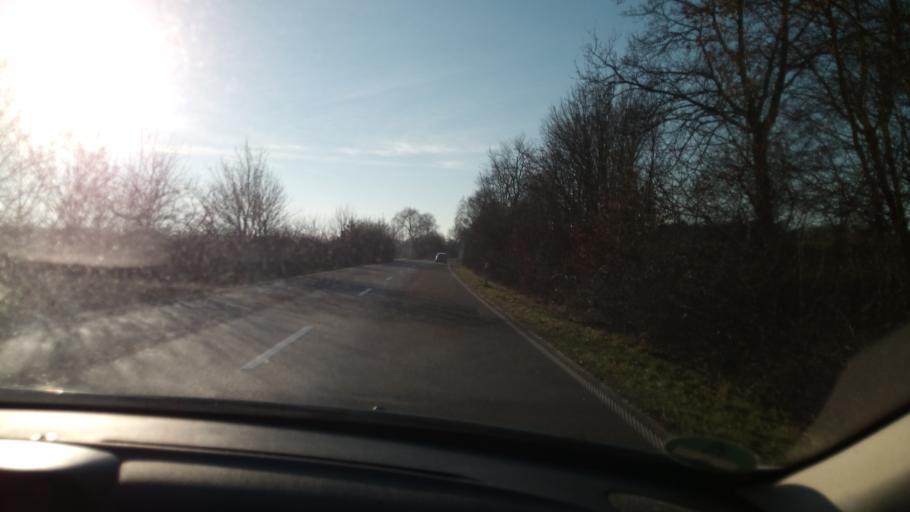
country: DE
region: Schleswig-Holstein
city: Witzeeze
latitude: 53.4575
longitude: 10.6207
